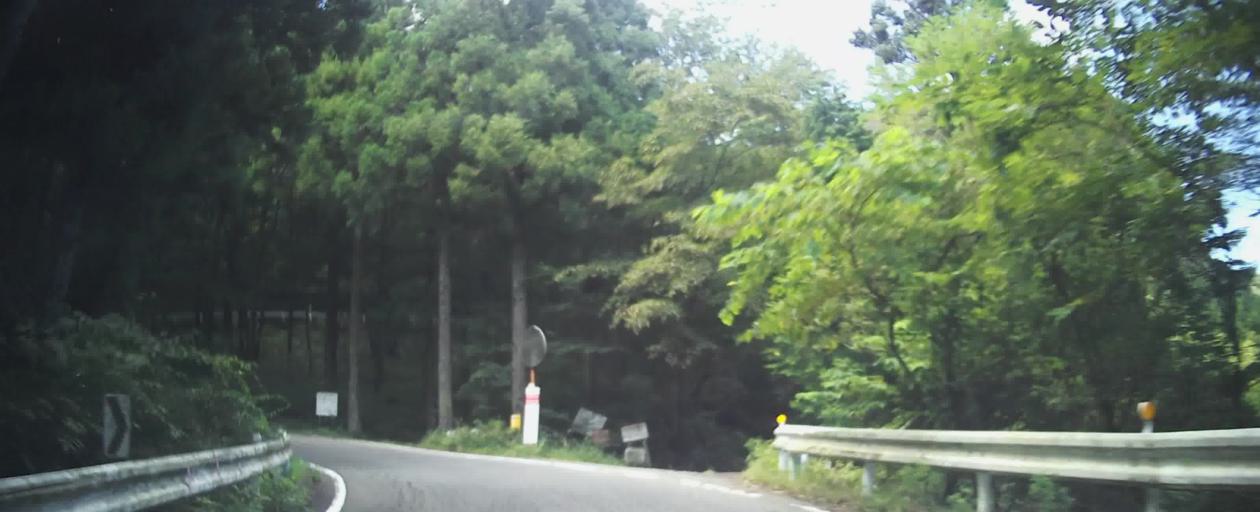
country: JP
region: Gunma
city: Shibukawa
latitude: 36.4590
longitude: 138.8974
